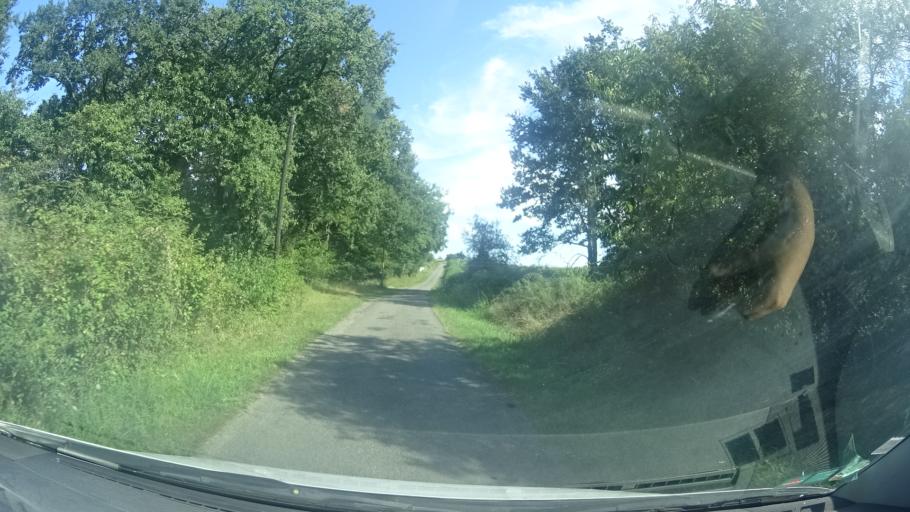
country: FR
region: Aquitaine
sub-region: Departement des Pyrenees-Atlantiques
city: Mont
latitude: 43.4950
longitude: -0.6675
